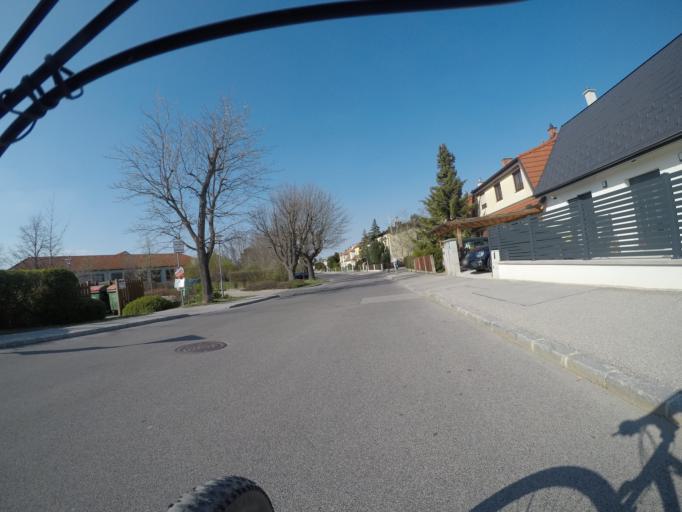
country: AT
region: Lower Austria
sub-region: Politischer Bezirk Modling
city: Neu-Guntramsdorf
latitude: 48.0628
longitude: 16.3223
